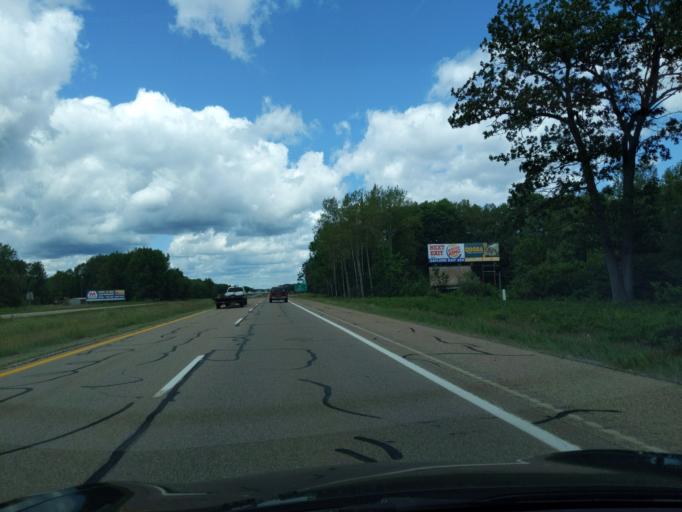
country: US
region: Michigan
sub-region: Roscommon County
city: Houghton Lake
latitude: 44.3276
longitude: -84.8071
